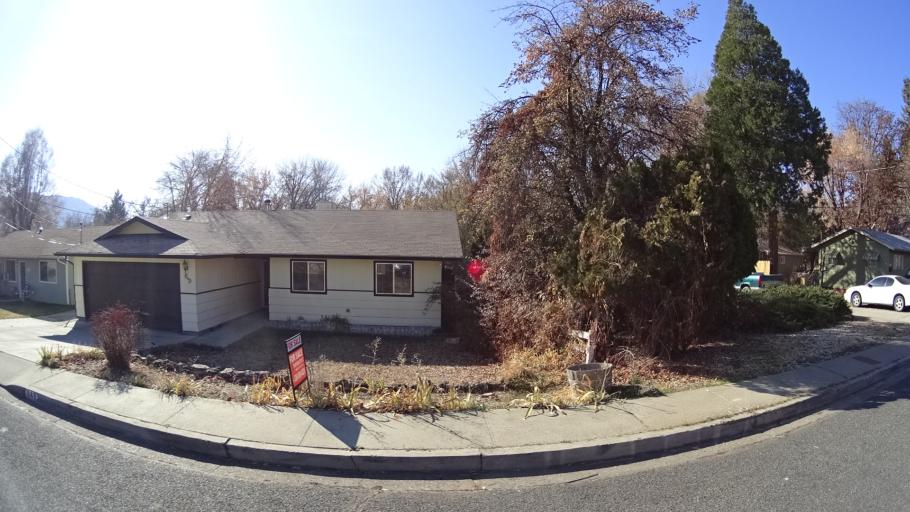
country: US
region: California
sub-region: Siskiyou County
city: Yreka
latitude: 41.7350
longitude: -122.6423
